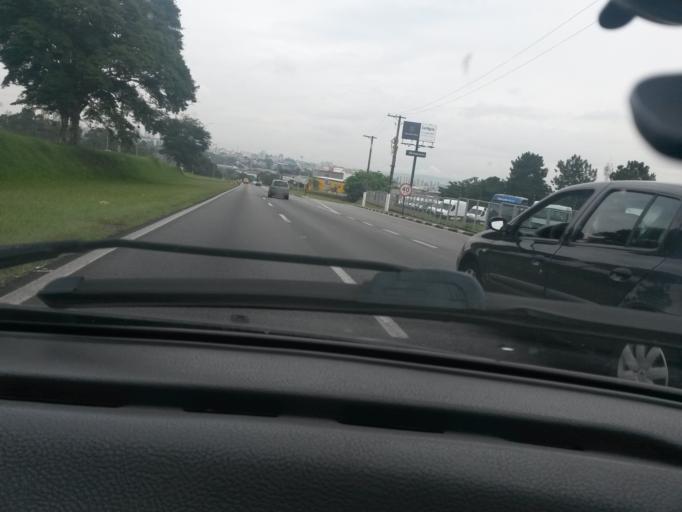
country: BR
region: Sao Paulo
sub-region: Sao Caetano Do Sul
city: Sao Caetano do Sul
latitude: -23.6504
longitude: -46.5804
